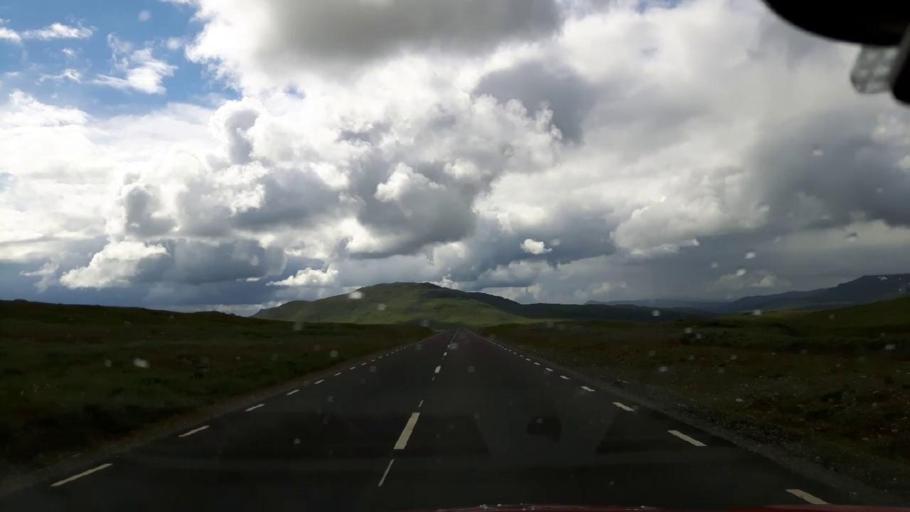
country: NO
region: Nordland
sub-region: Hattfjelldal
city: Hattfjelldal
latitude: 65.0427
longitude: 14.3298
